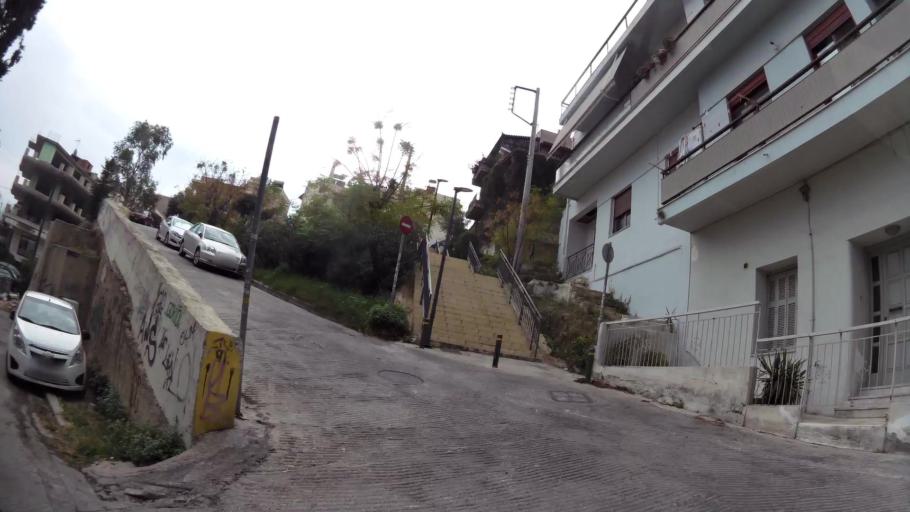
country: GR
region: Attica
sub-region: Nomarchia Athinas
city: Moskhaton
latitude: 37.9424
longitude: 23.6591
